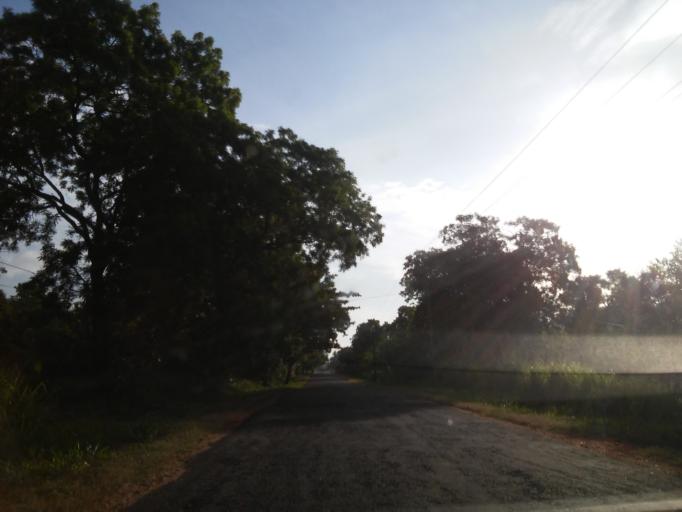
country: LK
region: Central
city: Sigiriya
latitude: 8.1645
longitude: 80.6577
